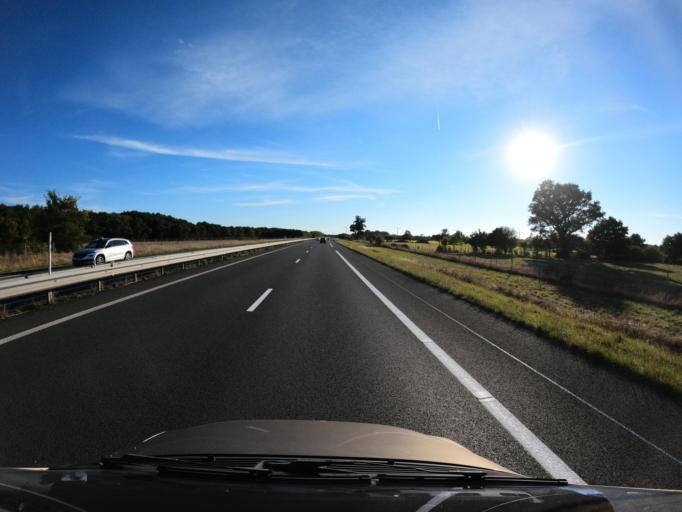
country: FR
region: Pays de la Loire
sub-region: Departement de Maine-et-Loire
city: Chemille-Melay
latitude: 47.2079
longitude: -0.7668
